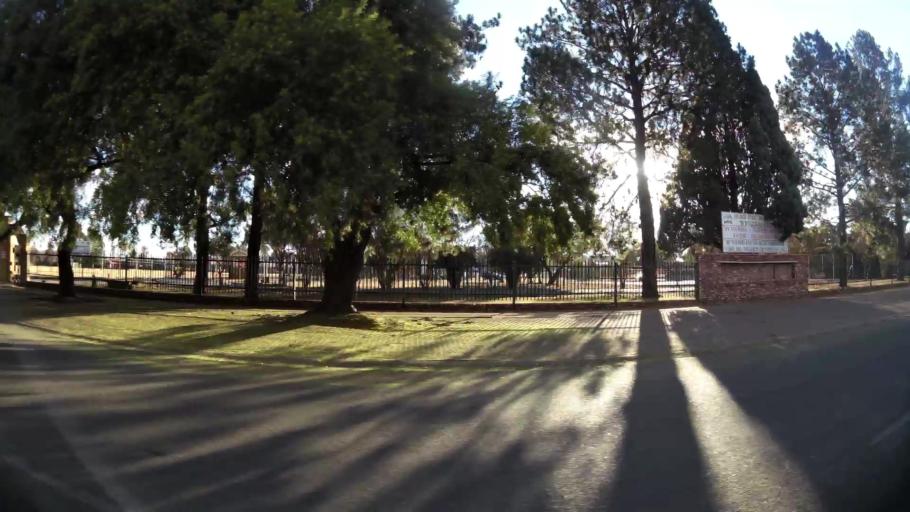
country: ZA
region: North-West
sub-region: Dr Kenneth Kaunda District Municipality
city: Potchefstroom
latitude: -26.7253
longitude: 27.0846
